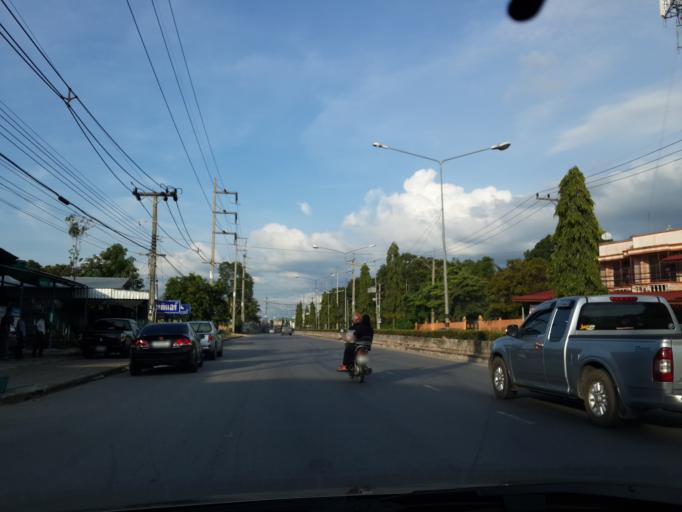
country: TH
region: Yala
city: Yala
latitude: 6.5444
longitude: 101.2720
